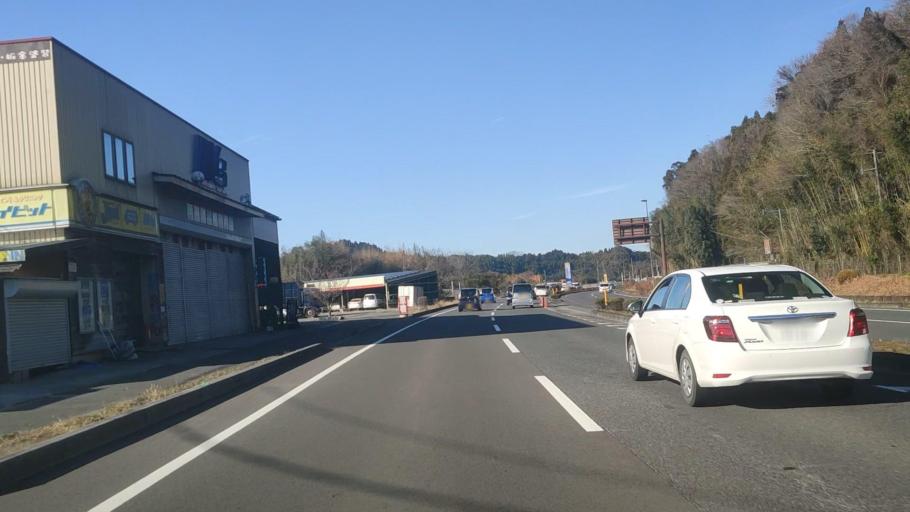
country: JP
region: Oita
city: Oita
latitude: 33.1147
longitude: 131.6546
